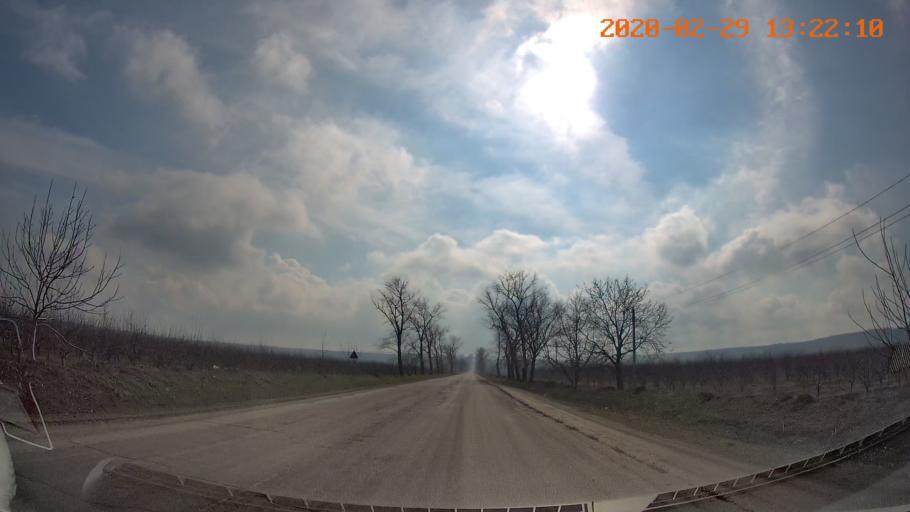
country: MD
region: Telenesti
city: Camenca
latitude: 47.9634
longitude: 28.6284
